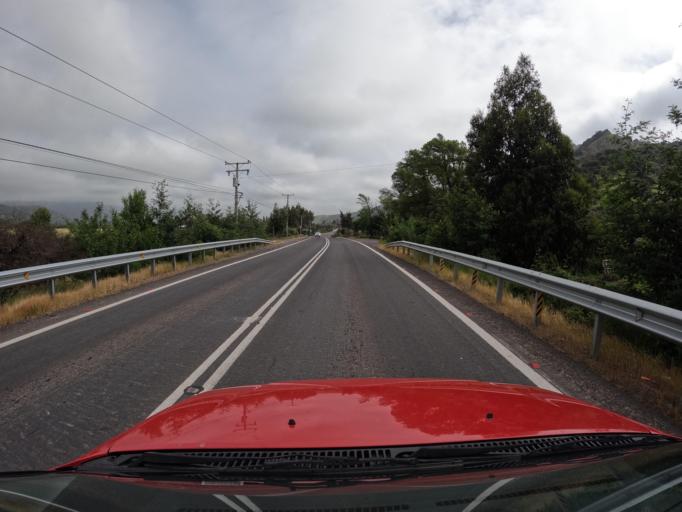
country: CL
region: Maule
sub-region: Provincia de Curico
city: Teno
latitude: -34.8165
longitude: -71.2116
